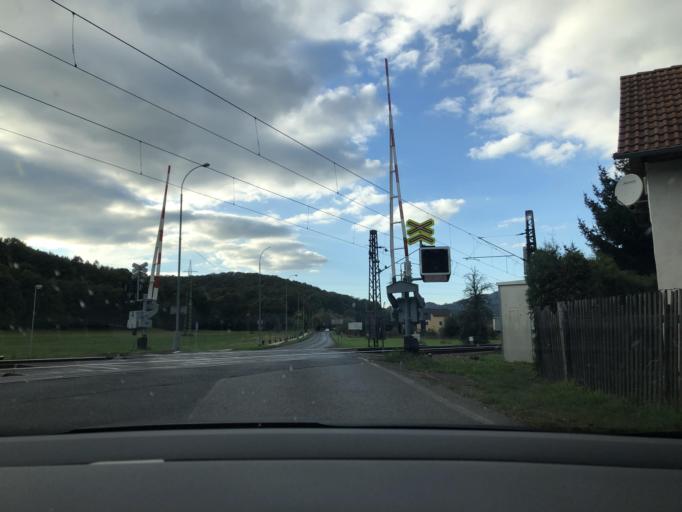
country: CZ
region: Ustecky
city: Velke Brezno
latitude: 50.6644
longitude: 14.1365
